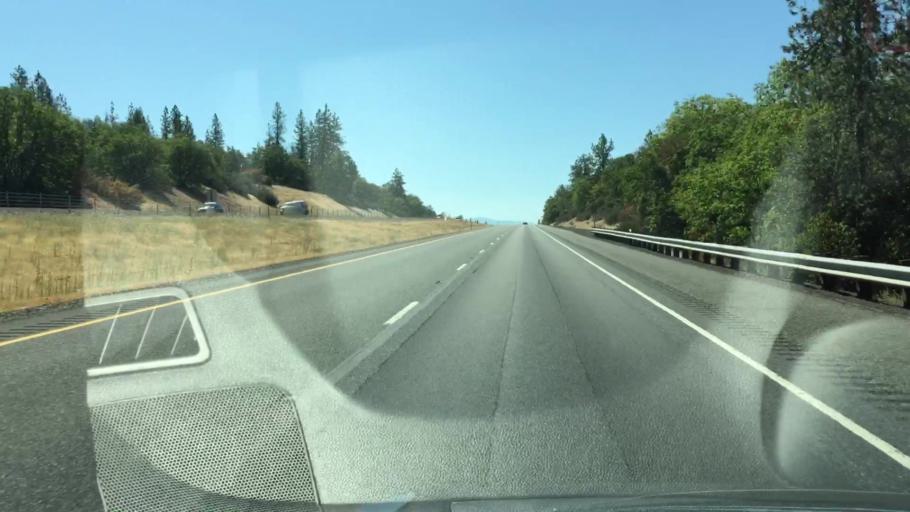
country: US
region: Oregon
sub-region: Josephine County
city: Merlin
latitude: 42.5464
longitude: -123.3708
